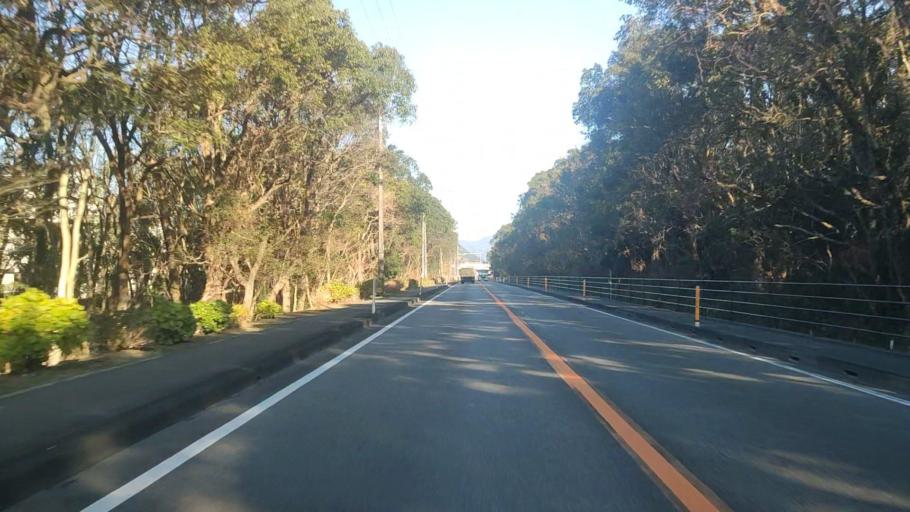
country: JP
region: Miyazaki
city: Nobeoka
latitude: 32.5318
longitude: 131.6809
